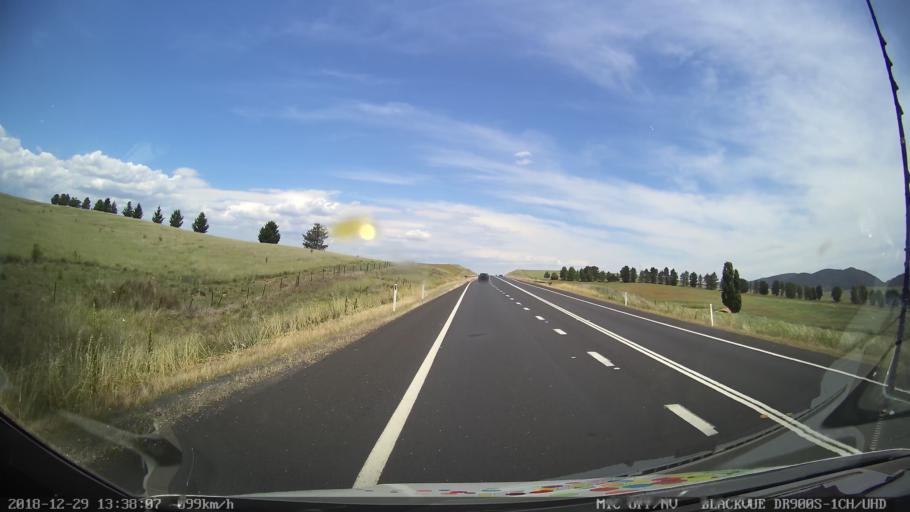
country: AU
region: New South Wales
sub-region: Cooma-Monaro
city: Cooma
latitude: -35.9940
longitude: 149.1399
